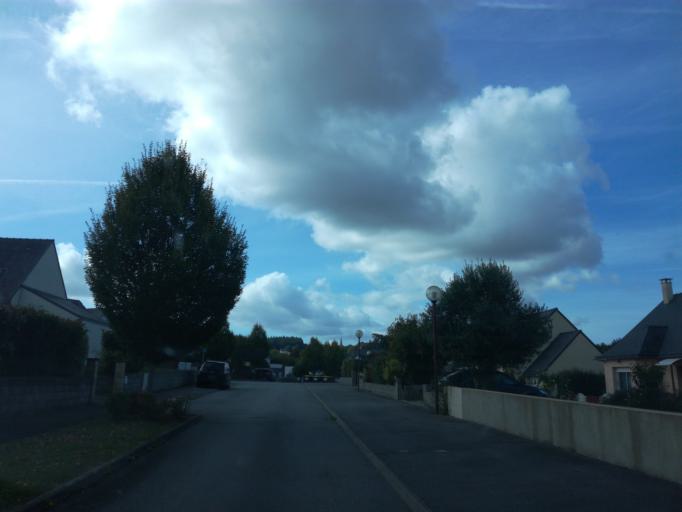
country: FR
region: Brittany
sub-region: Departement du Morbihan
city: Le Sourn
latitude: 48.0438
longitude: -2.9818
